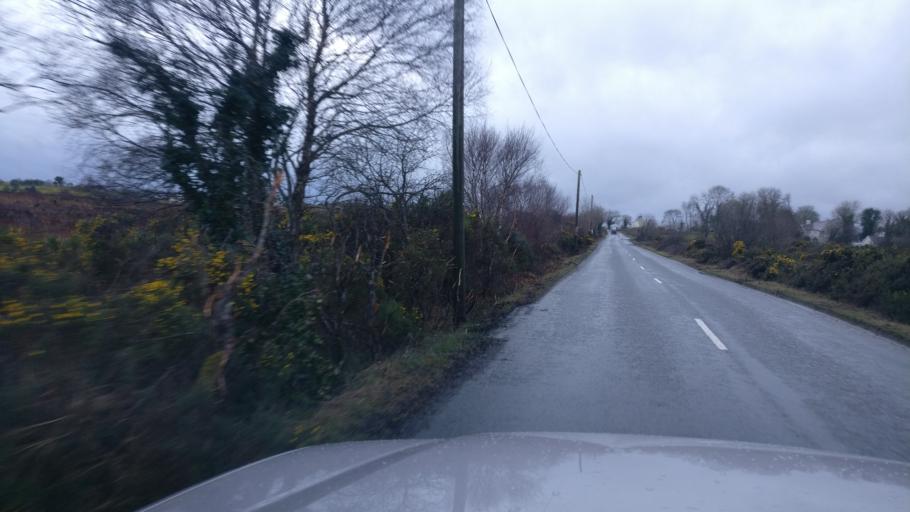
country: IE
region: Leinster
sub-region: An Iarmhi
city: Athlone
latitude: 53.4179
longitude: -8.0701
